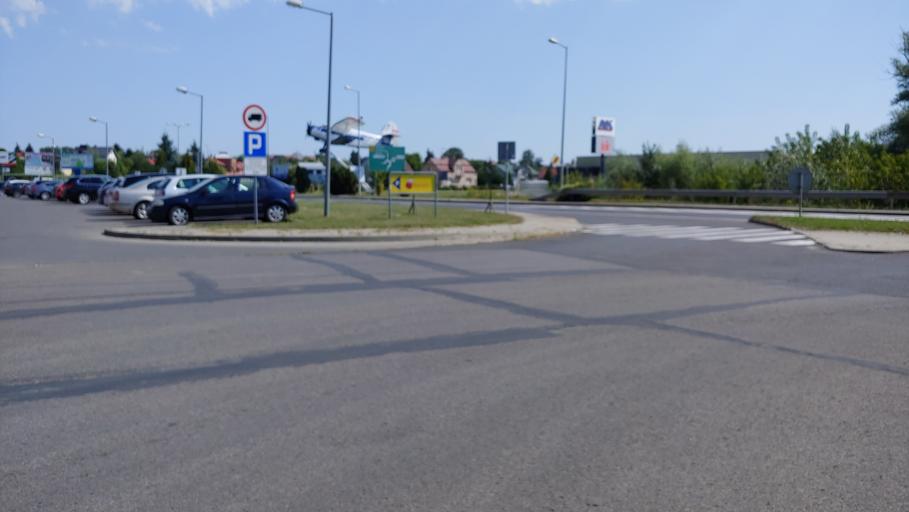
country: PL
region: Subcarpathian Voivodeship
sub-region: Powiat mielecki
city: Mielec
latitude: 50.2875
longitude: 21.4038
